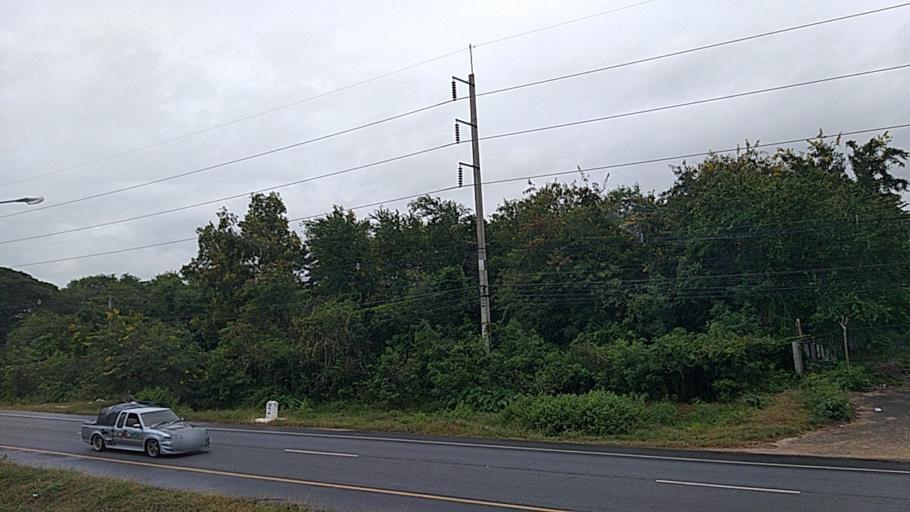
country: TH
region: Maha Sarakham
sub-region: Amphoe Borabue
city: Borabue
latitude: 16.0509
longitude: 103.1290
